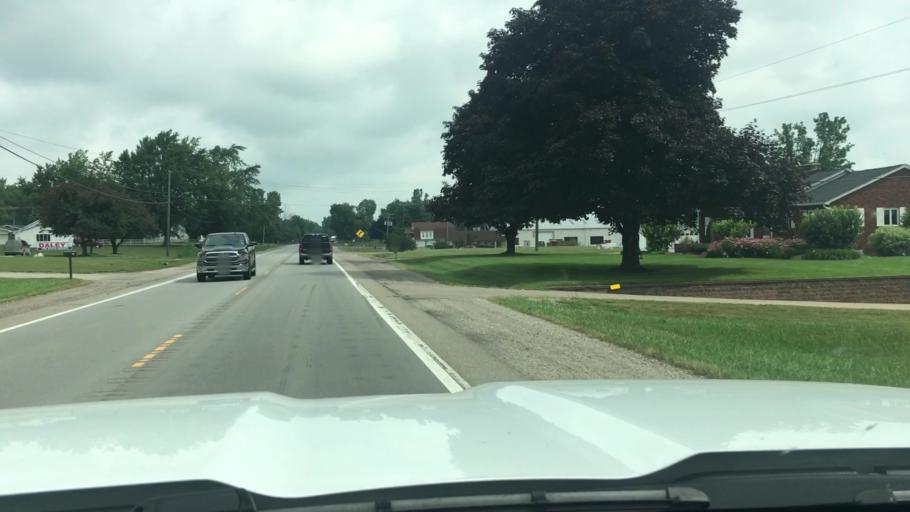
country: US
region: Michigan
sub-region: Lapeer County
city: Imlay City
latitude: 43.0443
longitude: -83.0723
